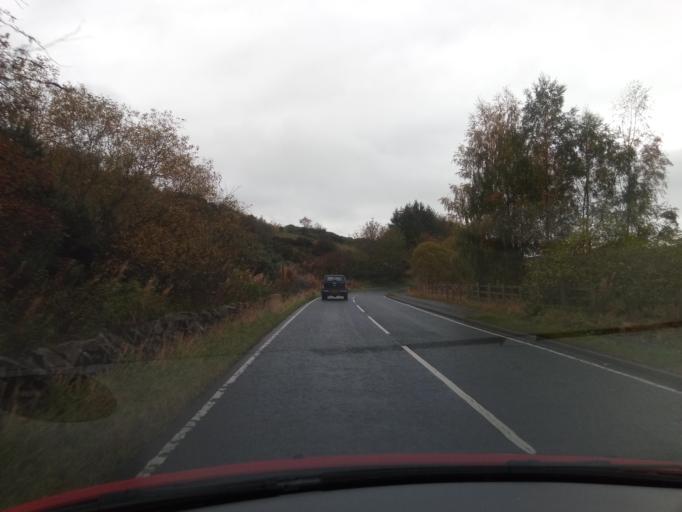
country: GB
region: Scotland
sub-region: The Scottish Borders
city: Galashiels
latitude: 55.6217
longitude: -2.8677
